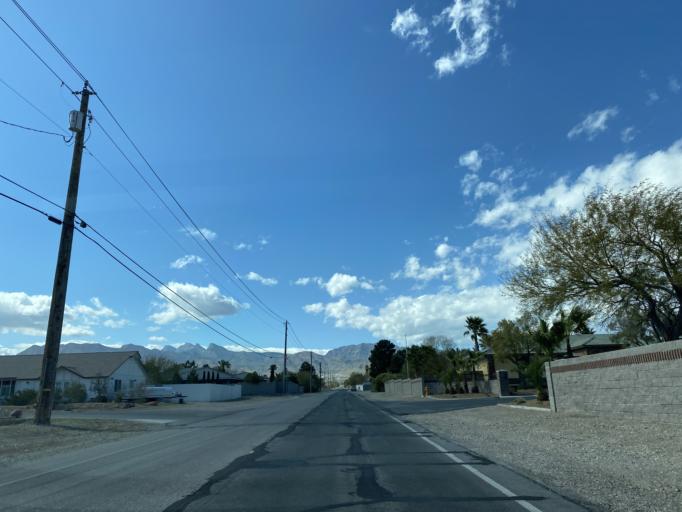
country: US
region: Nevada
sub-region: Clark County
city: Summerlin South
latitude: 36.2554
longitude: -115.2805
